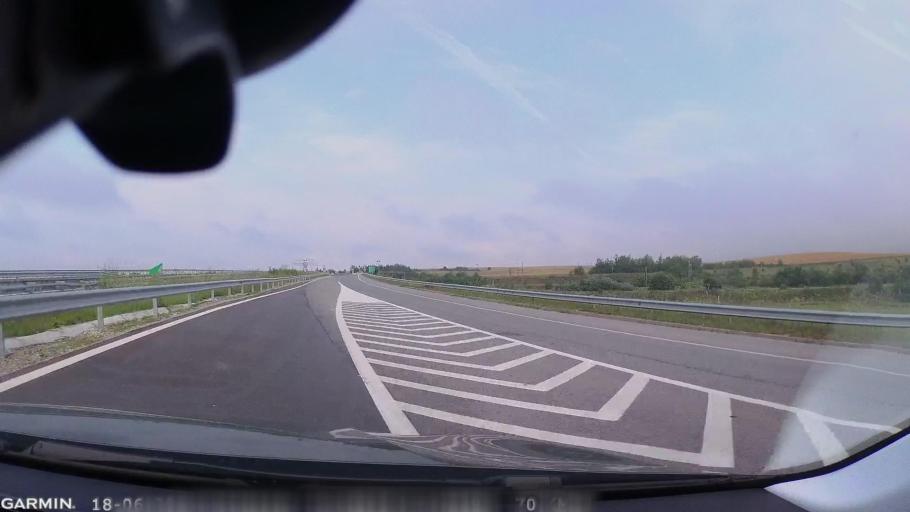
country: MK
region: Petrovec
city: Sredno Konjare
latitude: 41.9529
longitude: 21.7548
